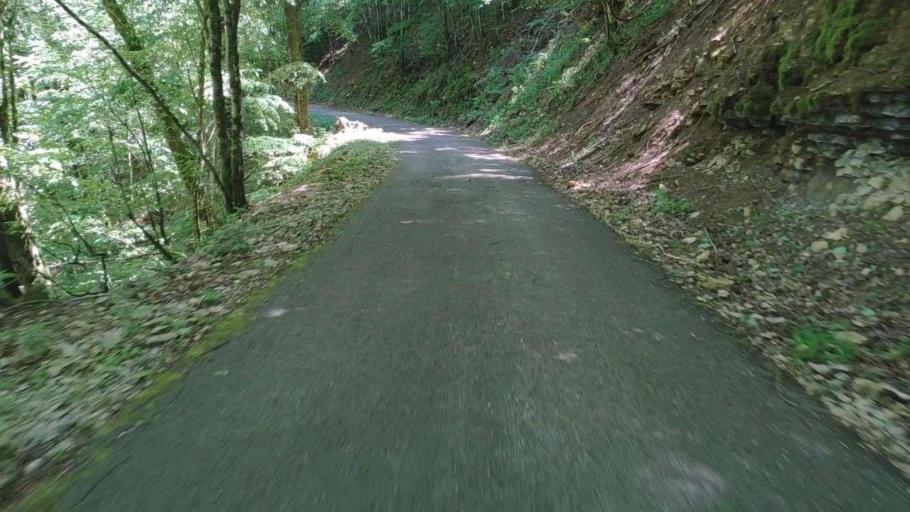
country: FR
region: Franche-Comte
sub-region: Departement du Jura
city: Poligny
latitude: 46.7455
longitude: 5.6778
